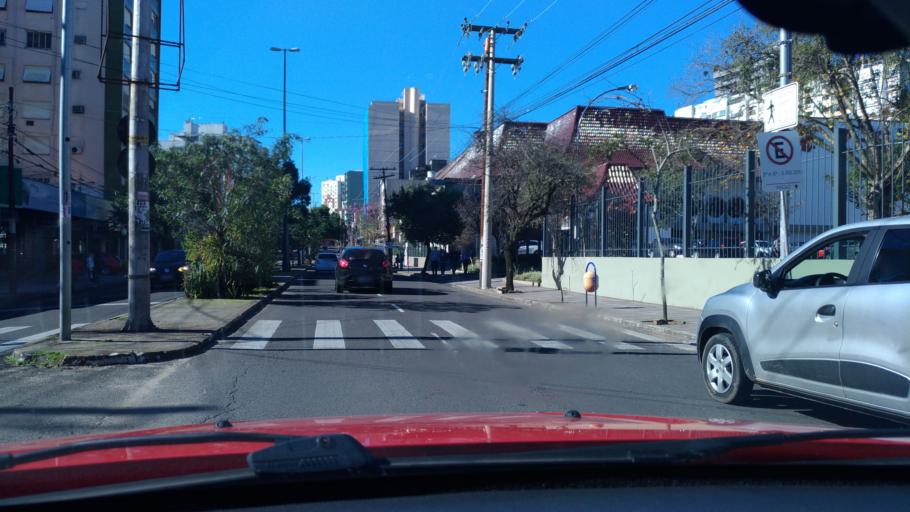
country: BR
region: Rio Grande do Sul
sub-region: Porto Alegre
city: Porto Alegre
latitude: -30.0213
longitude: -51.2079
